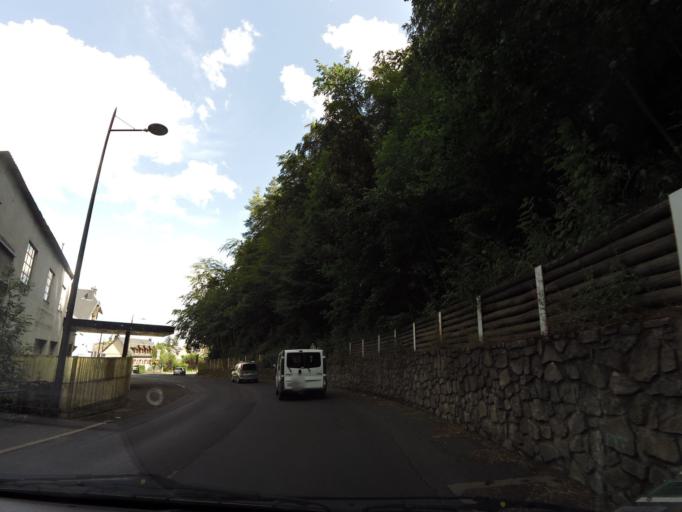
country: FR
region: Auvergne
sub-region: Departement du Puy-de-Dome
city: Aydat
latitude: 45.5748
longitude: 2.9382
